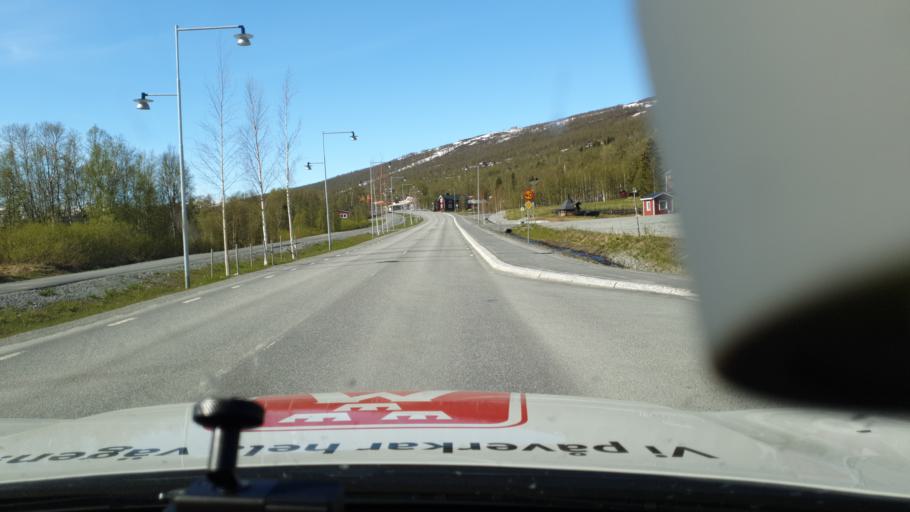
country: NO
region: Nordland
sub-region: Rana
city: Mo i Rana
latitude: 65.8151
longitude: 15.0877
